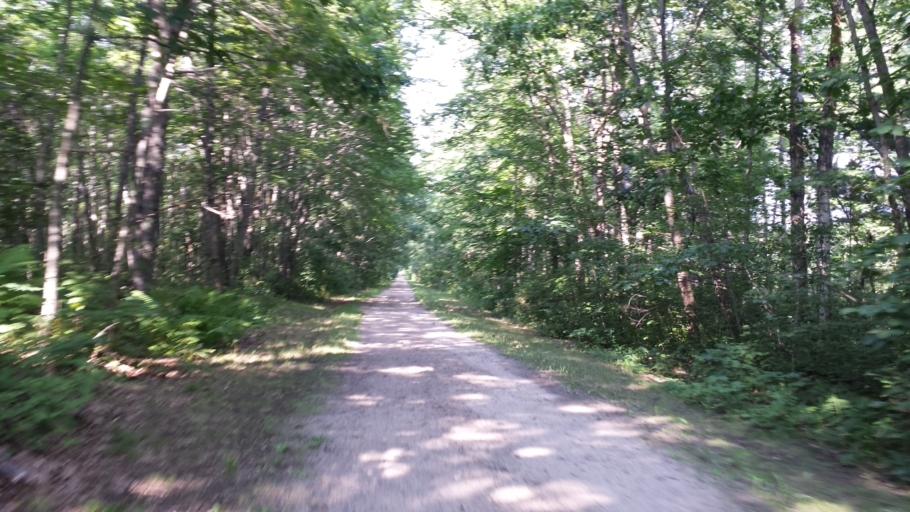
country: US
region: Maine
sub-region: York County
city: Biddeford
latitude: 43.4612
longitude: -70.5030
